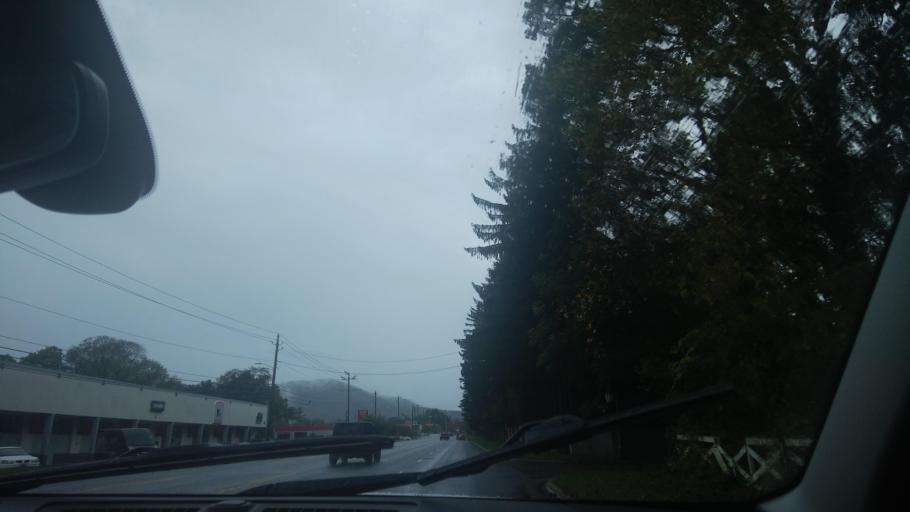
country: US
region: North Carolina
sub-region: Buncombe County
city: Biltmore Forest
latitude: 35.5515
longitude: -82.5375
